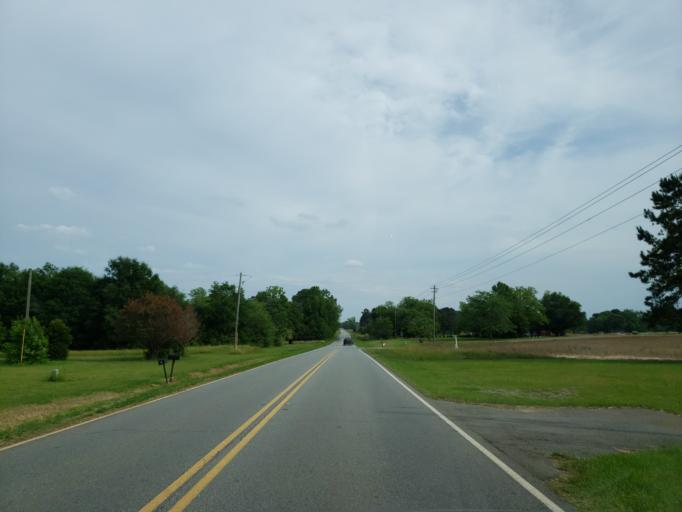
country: US
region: Georgia
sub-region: Dooly County
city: Vienna
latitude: 32.1360
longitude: -83.8720
